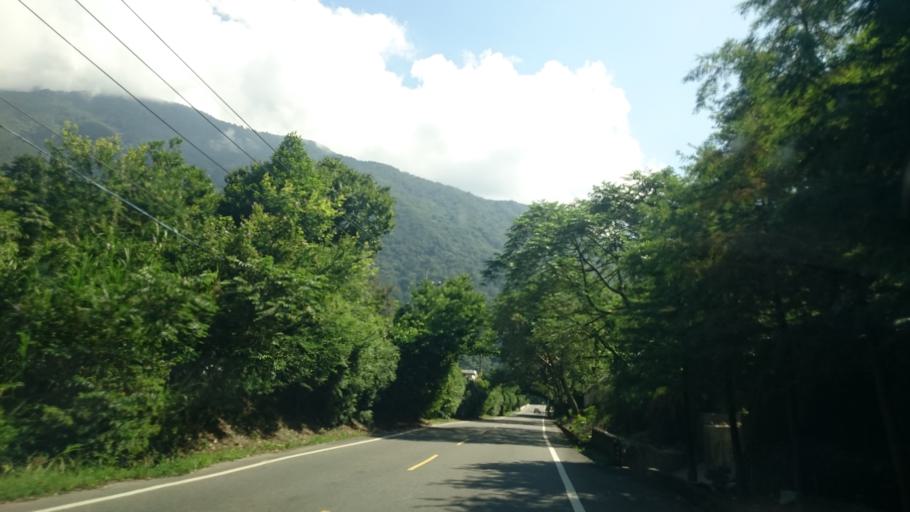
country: TW
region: Taiwan
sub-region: Nantou
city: Puli
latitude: 23.9983
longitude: 121.0508
